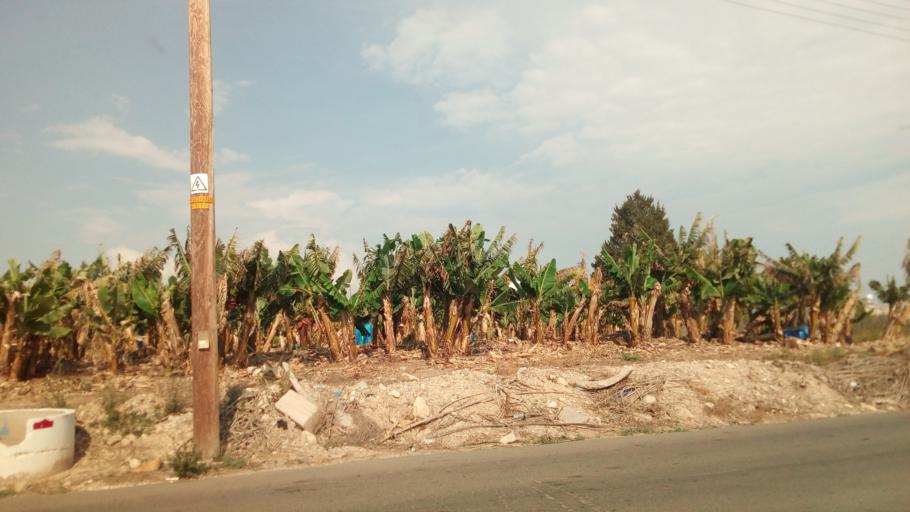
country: CY
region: Pafos
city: Pegeia
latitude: 34.8669
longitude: 32.3740
